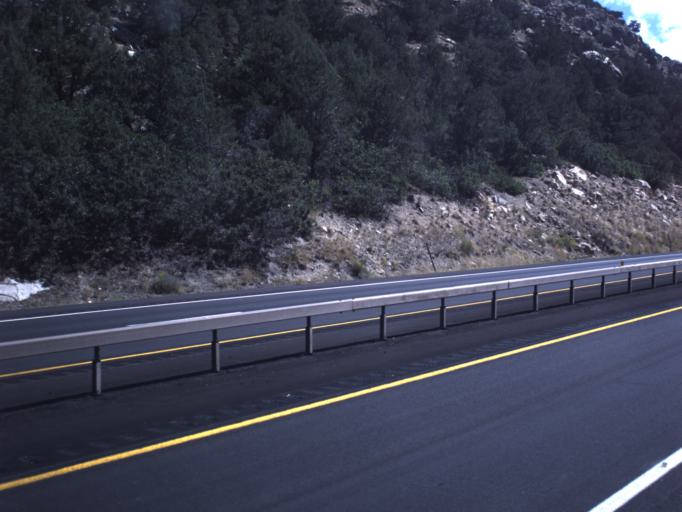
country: US
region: Utah
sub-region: Sevier County
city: Salina
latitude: 38.8906
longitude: -111.6143
